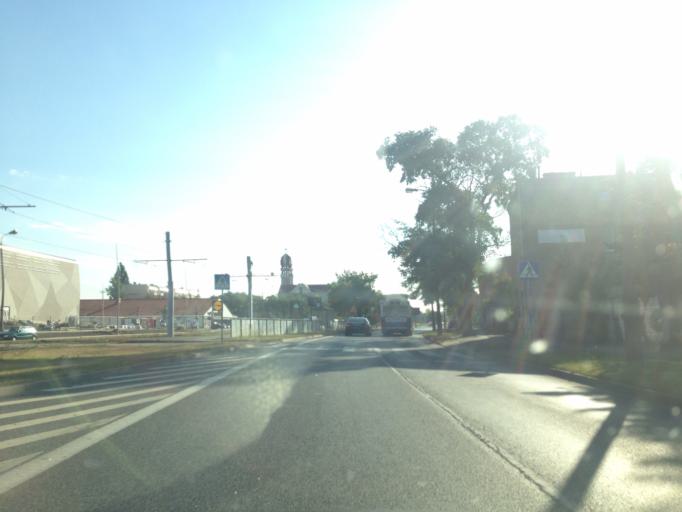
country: PL
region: Kujawsko-Pomorskie
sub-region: Bydgoszcz
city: Bydgoszcz
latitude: 53.1147
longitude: 18.0103
